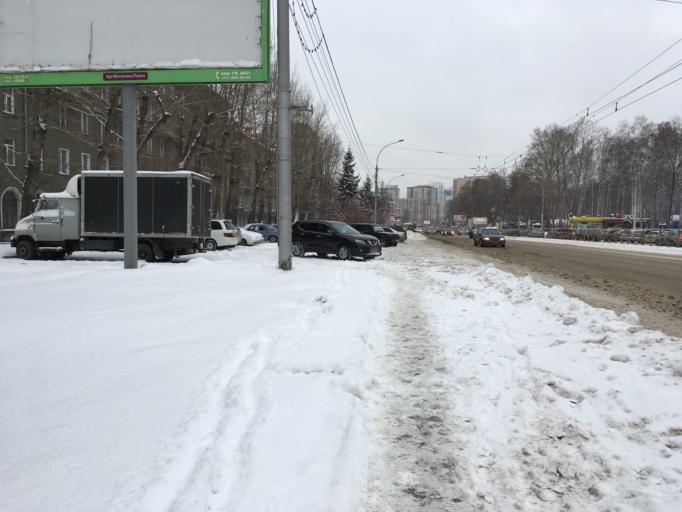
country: RU
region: Novosibirsk
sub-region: Novosibirskiy Rayon
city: Novosibirsk
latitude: 55.0475
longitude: 82.9584
